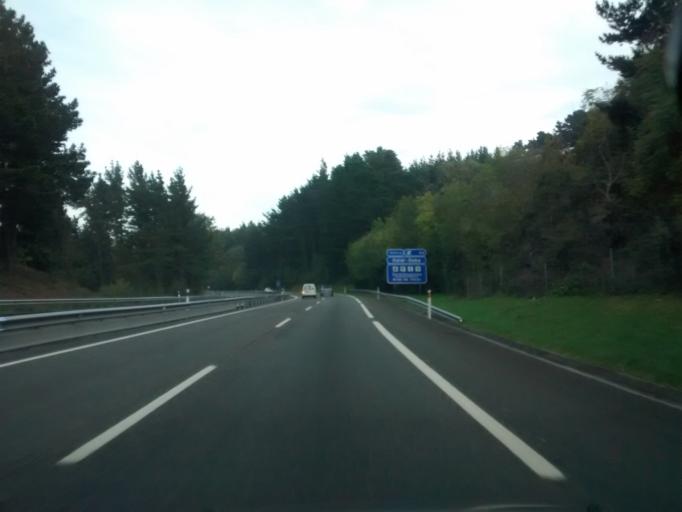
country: ES
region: Basque Country
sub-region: Provincia de Guipuzcoa
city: Deba
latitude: 43.2859
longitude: -2.3520
